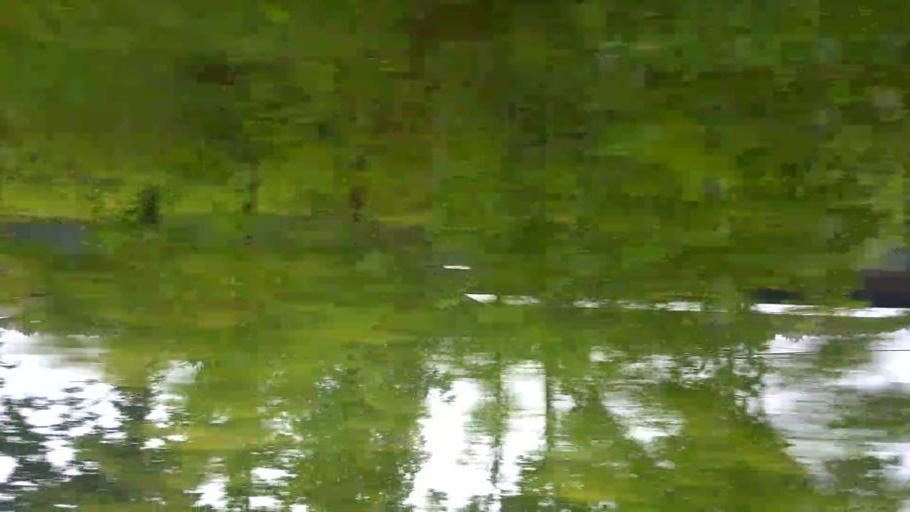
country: RU
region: Moskovskaya
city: Ozherel'ye
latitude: 54.8383
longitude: 38.2743
